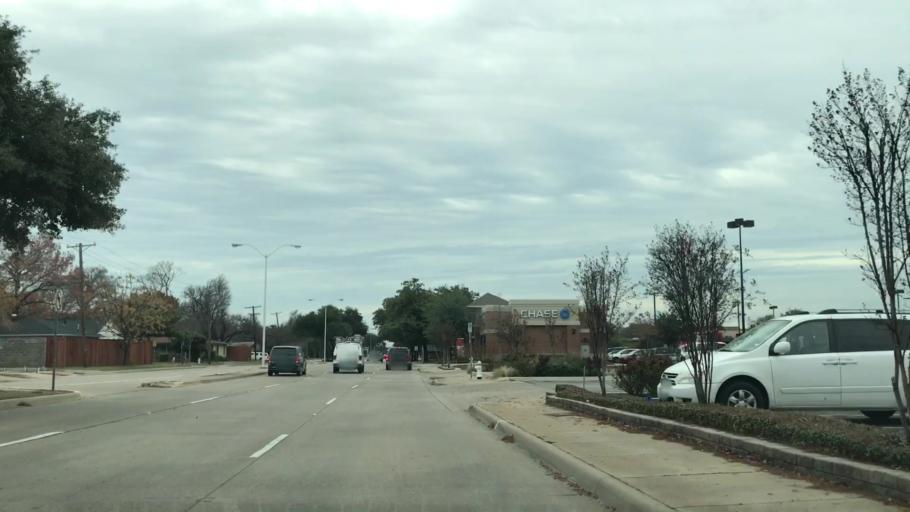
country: US
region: Texas
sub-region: Dallas County
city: Farmers Branch
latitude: 32.9229
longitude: -96.8817
